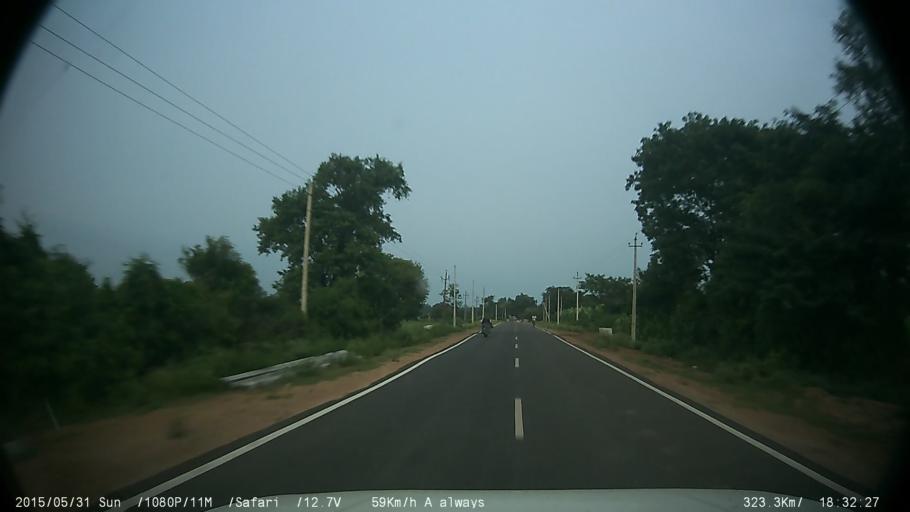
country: IN
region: Karnataka
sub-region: Mysore
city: Nanjangud
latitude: 12.1343
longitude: 76.7472
